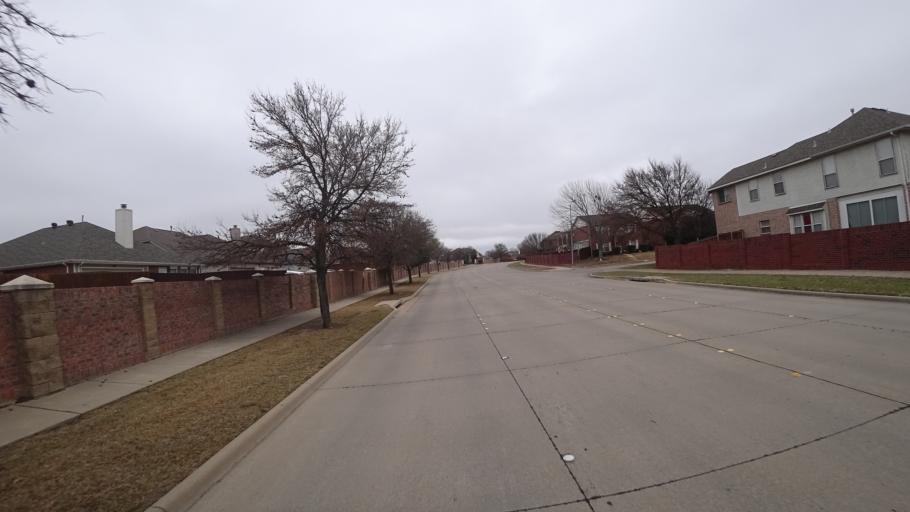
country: US
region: Texas
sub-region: Denton County
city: Lewisville
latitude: 33.0359
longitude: -97.0339
